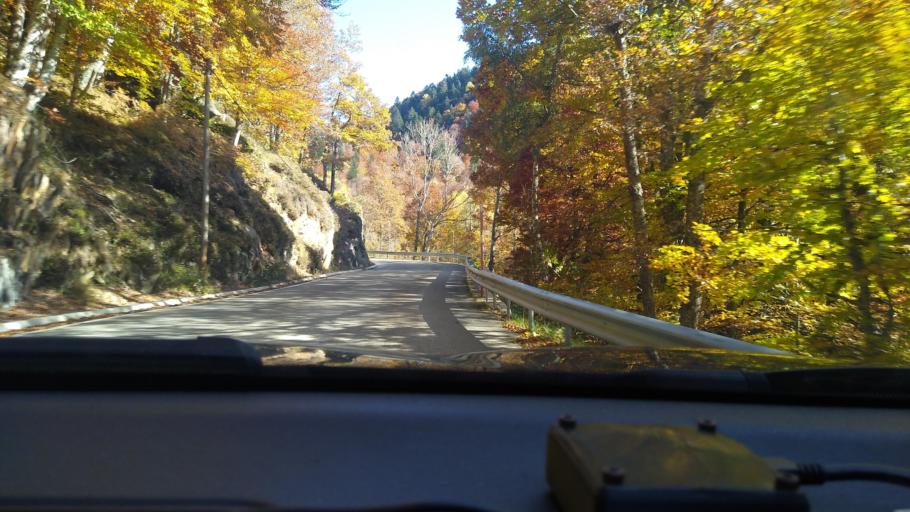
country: FR
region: Midi-Pyrenees
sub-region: Departement de l'Ariege
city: Ax-les-Thermes
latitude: 42.7171
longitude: 1.9274
